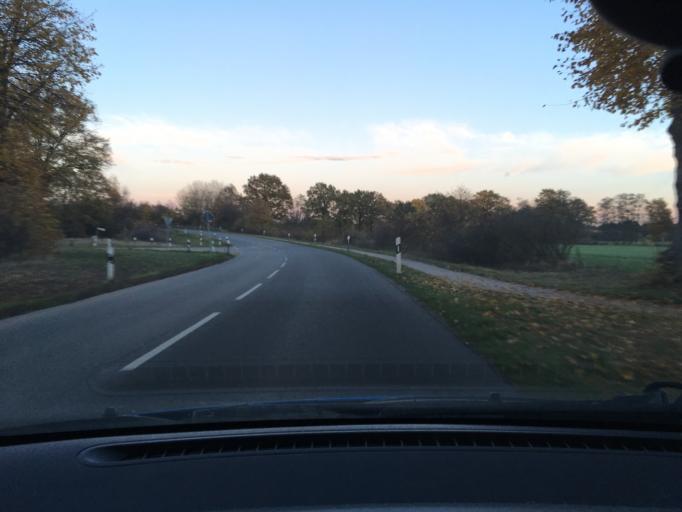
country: DE
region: Lower Saxony
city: Radbruch
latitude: 53.3213
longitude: 10.2943
